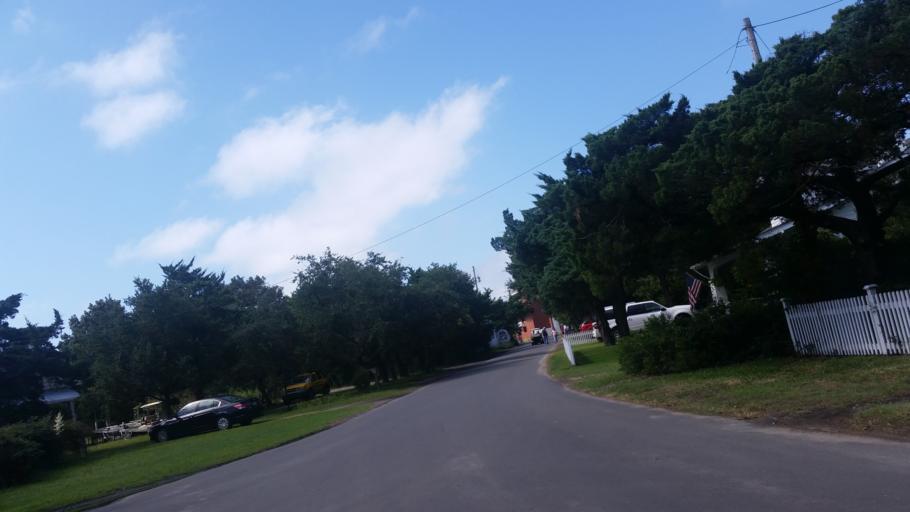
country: US
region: North Carolina
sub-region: Hyde County
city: Swanquarter
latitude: 35.1157
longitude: -75.9821
